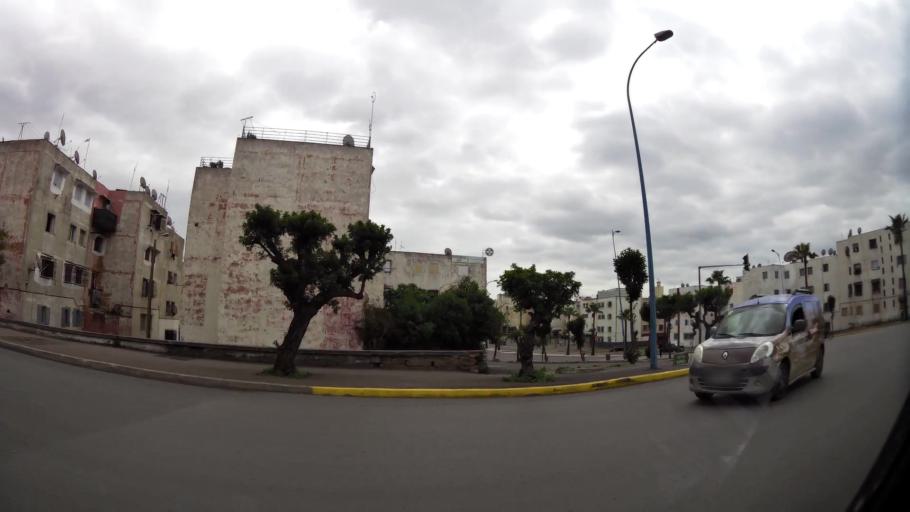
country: MA
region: Grand Casablanca
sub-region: Casablanca
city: Casablanca
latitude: 33.5773
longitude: -7.5664
